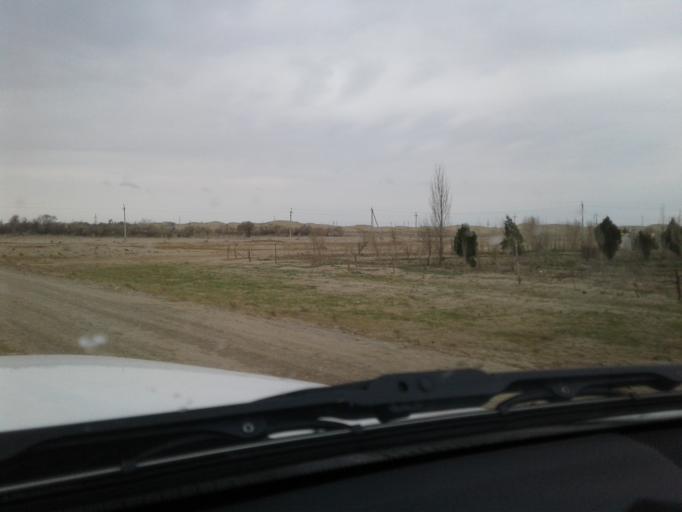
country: TM
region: Ahal
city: Abadan
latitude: 38.7574
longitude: 58.4911
